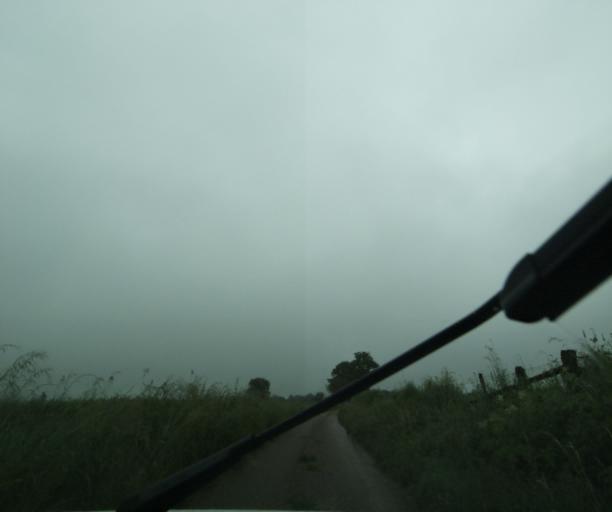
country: FR
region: Bourgogne
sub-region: Departement de Saone-et-Loire
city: Charolles
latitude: 46.3898
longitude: 4.3627
